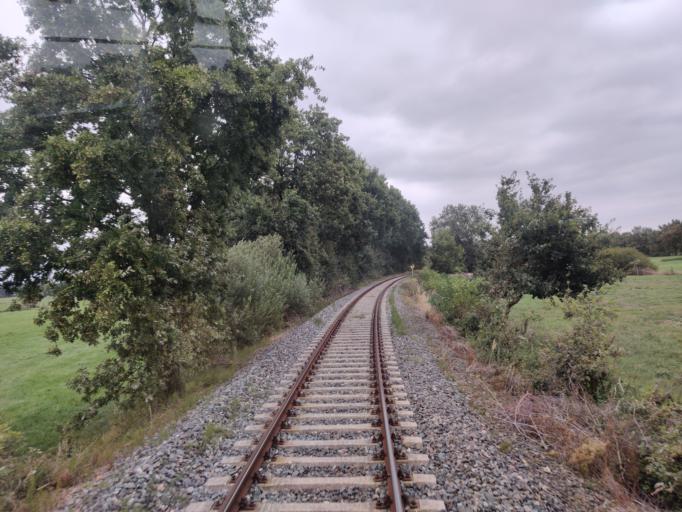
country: DE
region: Lower Saxony
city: Gnarrenburg
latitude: 53.3346
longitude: 8.9819
